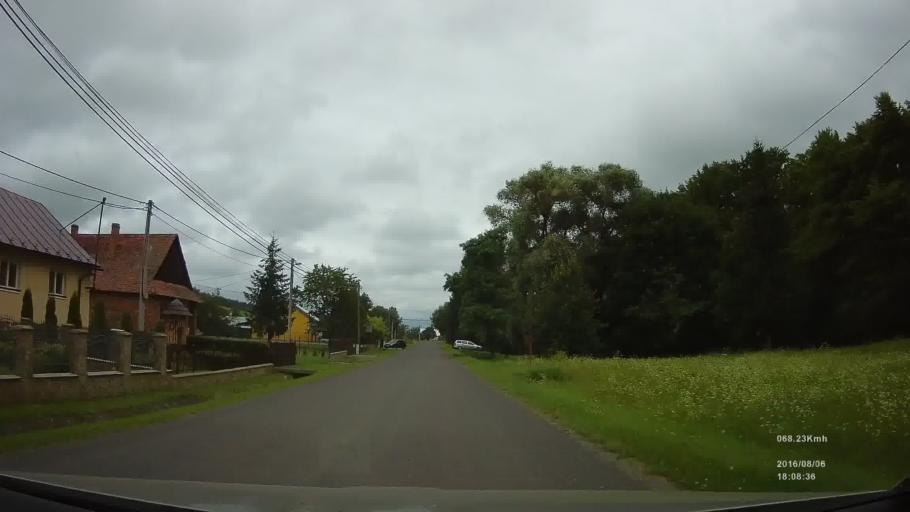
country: SK
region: Presovsky
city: Svidnik
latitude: 49.3853
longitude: 21.5677
